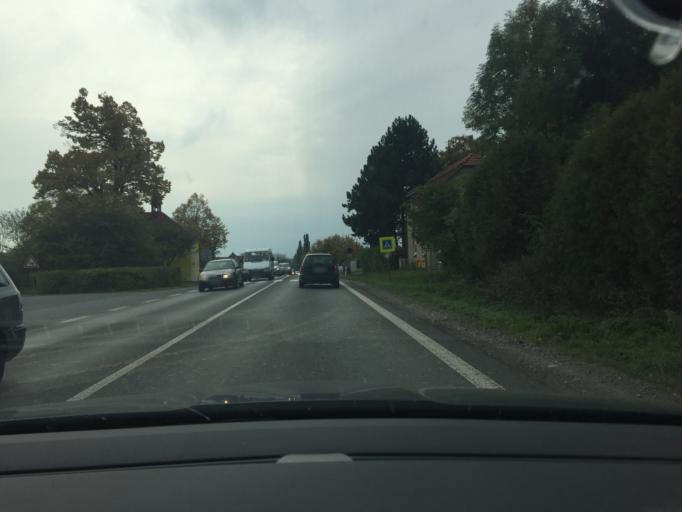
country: CZ
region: Central Bohemia
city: Milin
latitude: 49.5725
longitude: 14.0777
